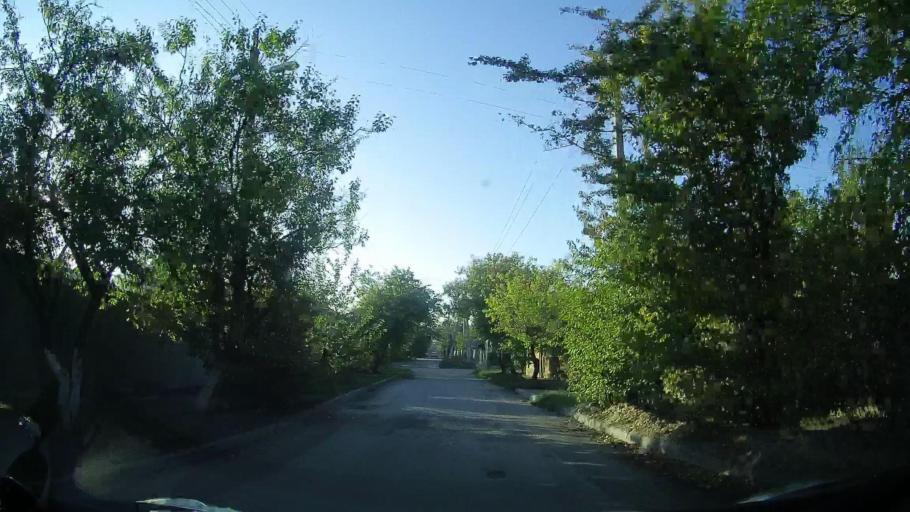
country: RU
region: Rostov
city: Severnyy
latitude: 47.2672
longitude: 39.6796
